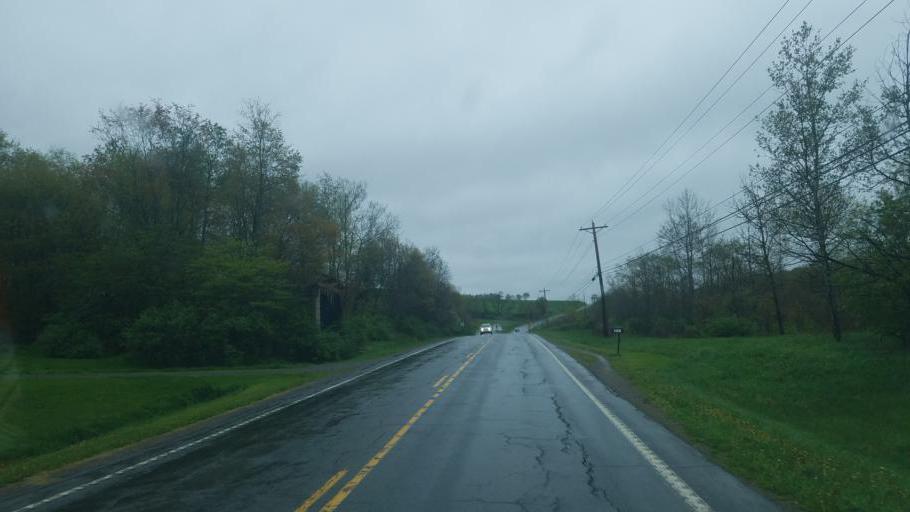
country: US
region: Pennsylvania
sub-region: Potter County
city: Galeton
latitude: 41.8898
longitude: -77.7948
